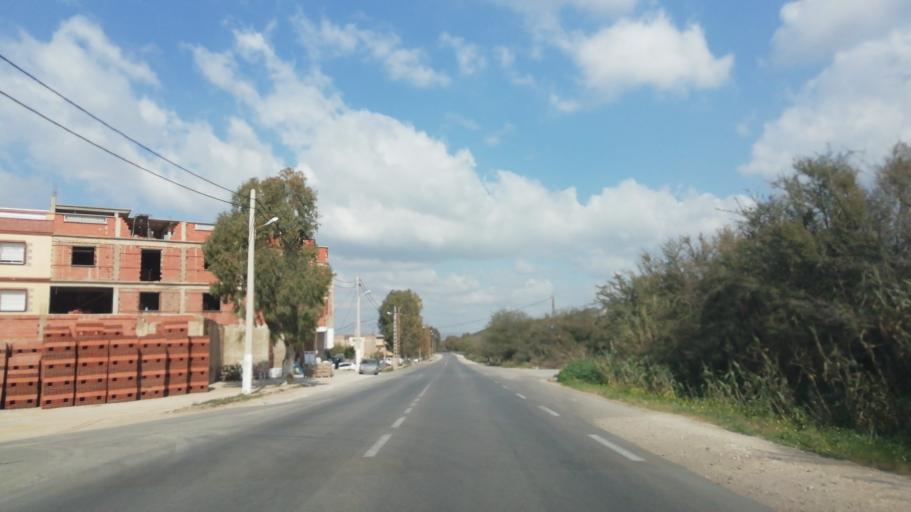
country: DZ
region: Mostaganem
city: Mostaganem
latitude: 35.6840
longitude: 0.2068
